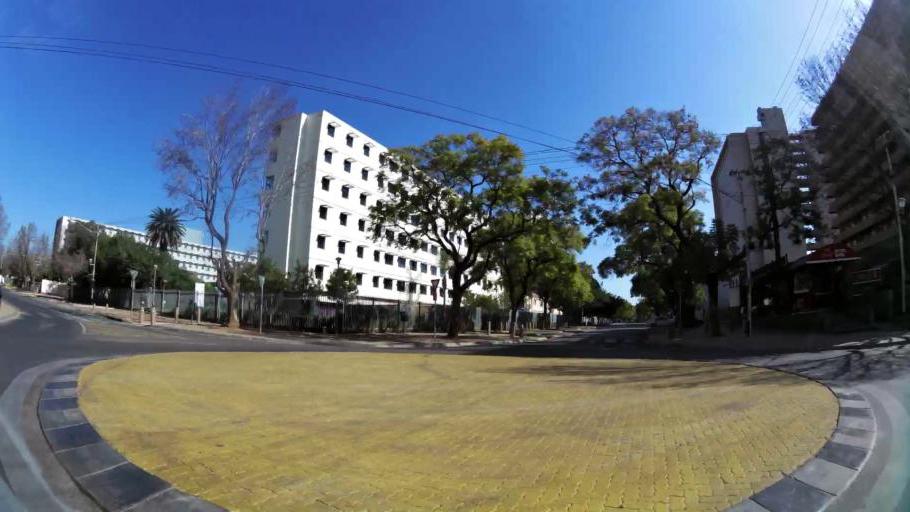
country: ZA
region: Gauteng
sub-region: City of Tshwane Metropolitan Municipality
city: Pretoria
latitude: -25.7520
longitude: 28.2354
